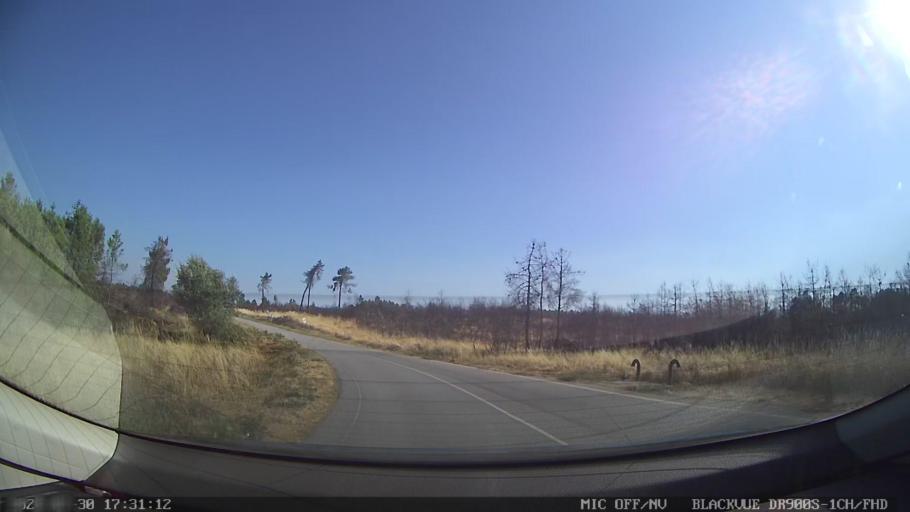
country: PT
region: Vila Real
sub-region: Murca
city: Murca
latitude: 41.3424
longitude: -7.4730
